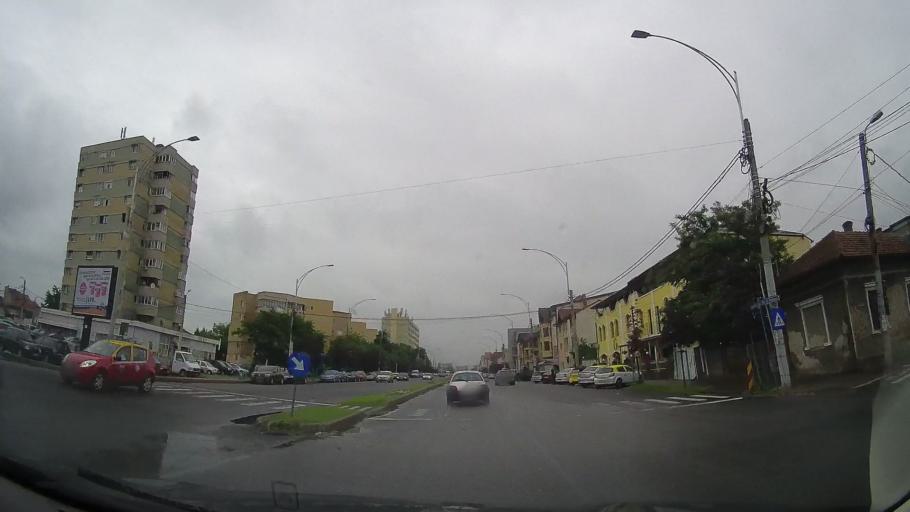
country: RO
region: Mehedinti
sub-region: Municipiul Drobeta-Turnu Severin
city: Drobeta-Turnu Severin
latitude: 44.6306
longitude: 22.6424
